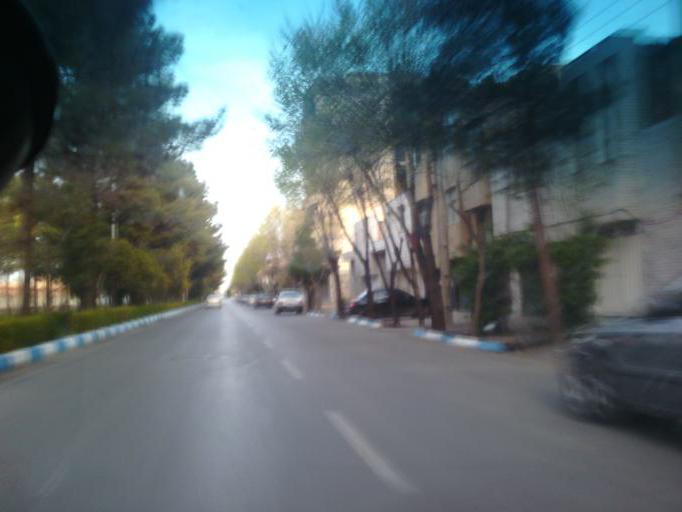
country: IR
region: Isfahan
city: Shahin Shahr
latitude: 32.8752
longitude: 51.5501
